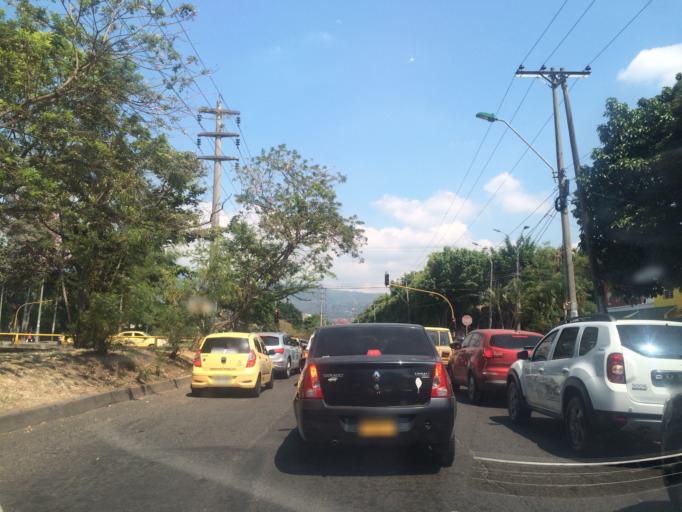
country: CO
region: Valle del Cauca
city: Cali
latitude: 3.4075
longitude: -76.5298
